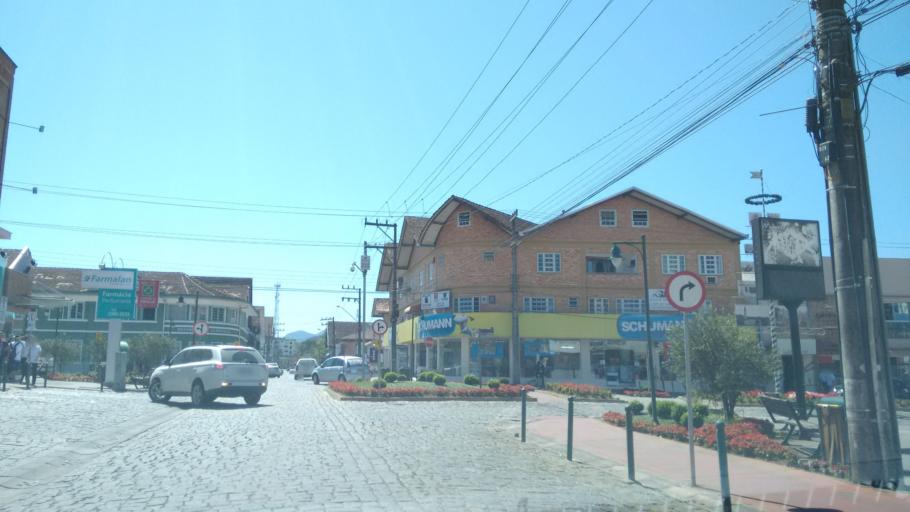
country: BR
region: Santa Catarina
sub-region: Pomerode
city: Pomerode
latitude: -26.7376
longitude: -49.1765
